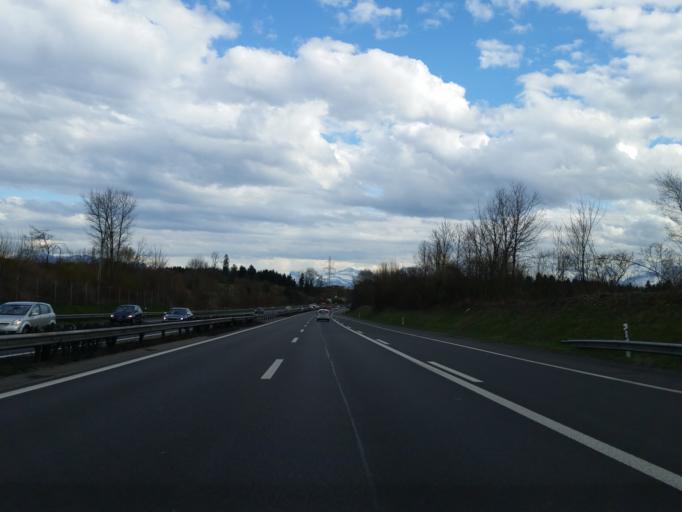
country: CH
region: Lucerne
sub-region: Sursee District
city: Neuenkirch
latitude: 47.1096
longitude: 8.2364
